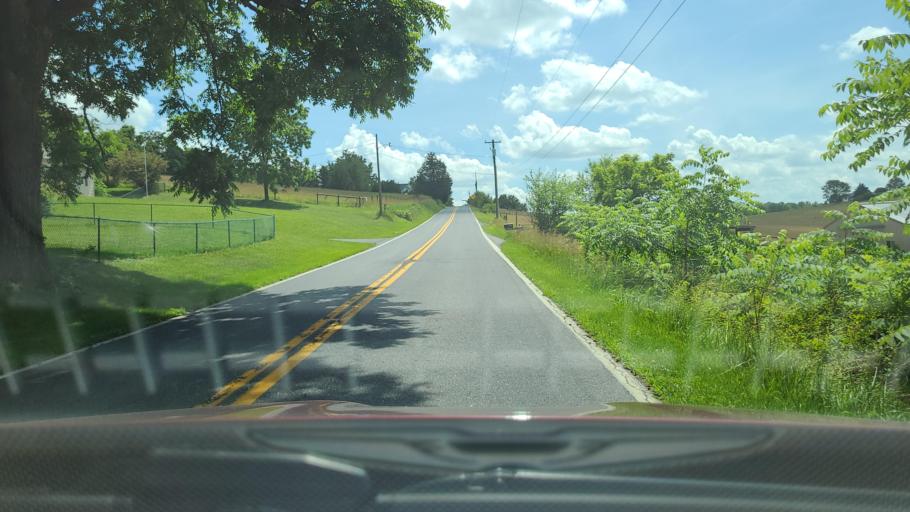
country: US
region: Maryland
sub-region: Montgomery County
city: Clarksburg
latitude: 39.2634
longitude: -77.2573
